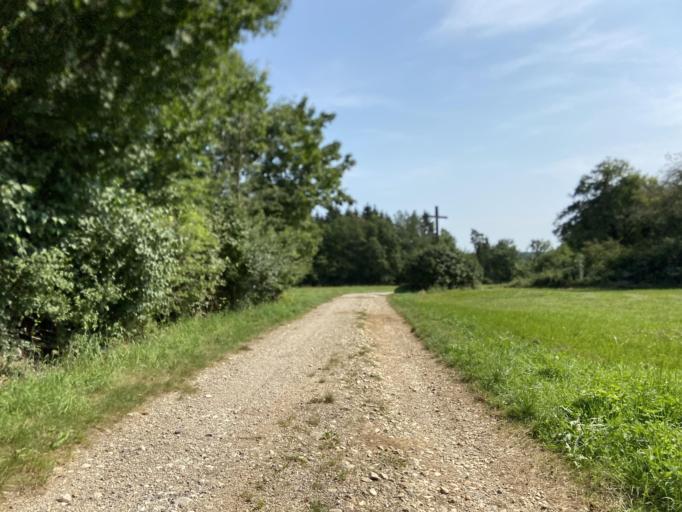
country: DE
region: Baden-Wuerttemberg
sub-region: Tuebingen Region
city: Scheer
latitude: 48.0750
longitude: 9.2785
